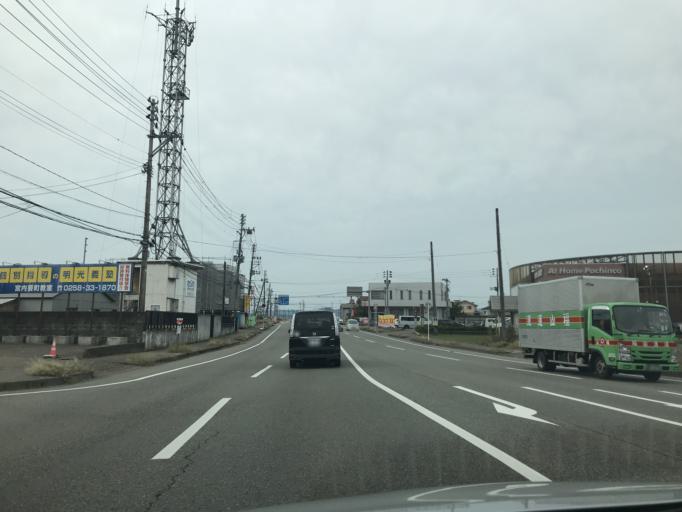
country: JP
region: Niigata
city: Nagaoka
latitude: 37.4264
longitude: 138.8386
